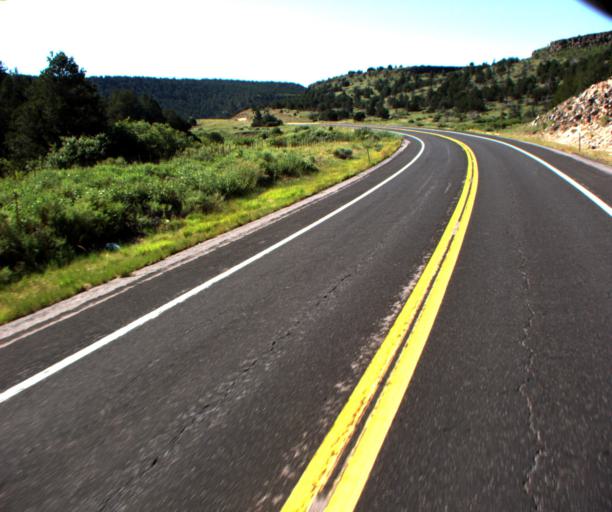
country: US
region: Arizona
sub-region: Apache County
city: Eagar
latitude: 34.0853
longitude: -109.2032
